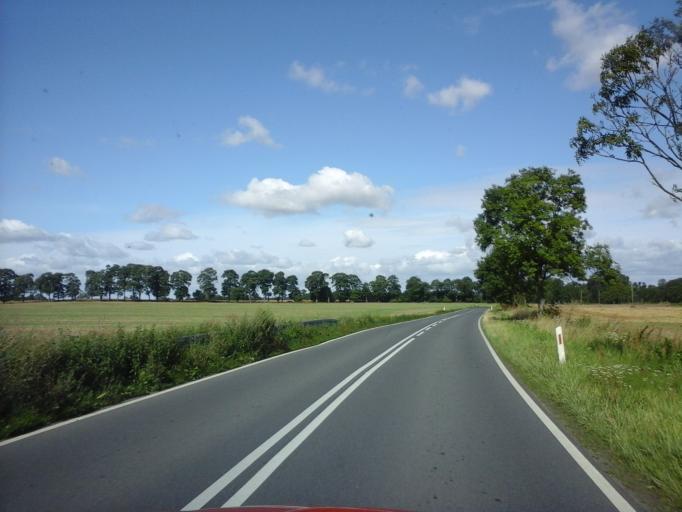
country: PL
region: West Pomeranian Voivodeship
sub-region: Powiat stargardzki
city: Dolice
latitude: 53.2030
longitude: 15.1527
